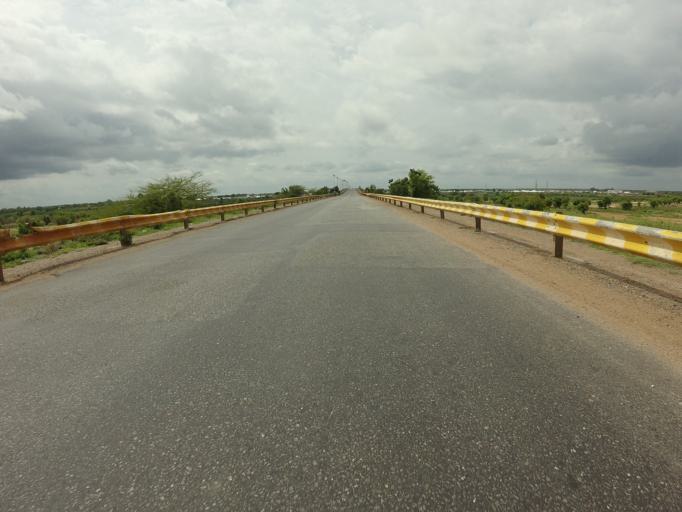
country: GH
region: Brong-Ahafo
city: Kintampo
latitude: 8.7607
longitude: -1.4549
